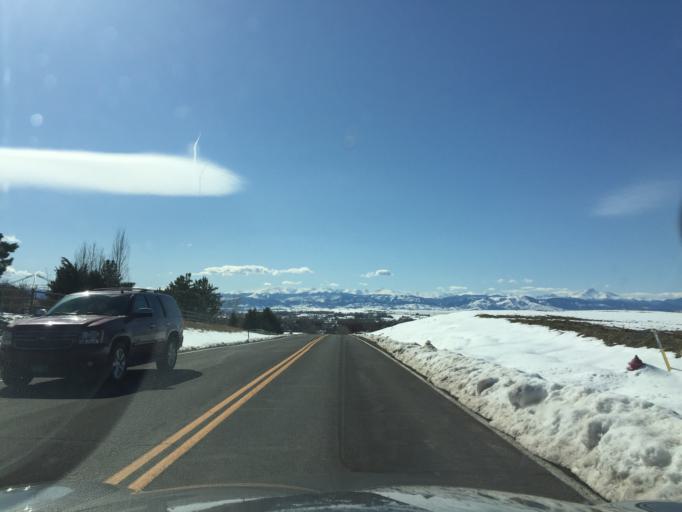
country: US
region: Colorado
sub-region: Boulder County
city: Erie
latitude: 40.0658
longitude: -105.0456
